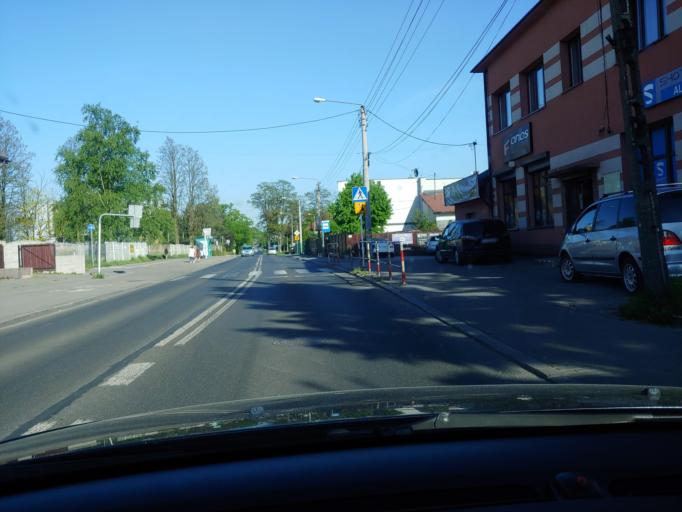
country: PL
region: Silesian Voivodeship
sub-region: Jaworzno
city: Jaworzno
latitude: 50.1975
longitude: 19.2793
